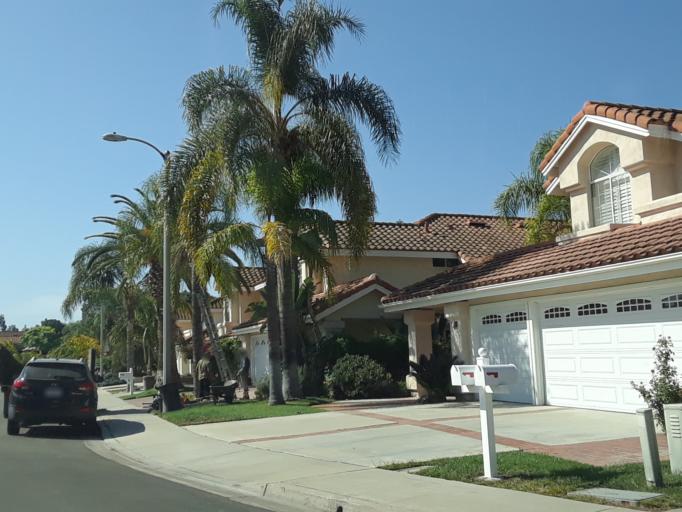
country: US
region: California
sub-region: Orange County
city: Irvine
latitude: 33.6772
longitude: -117.8188
